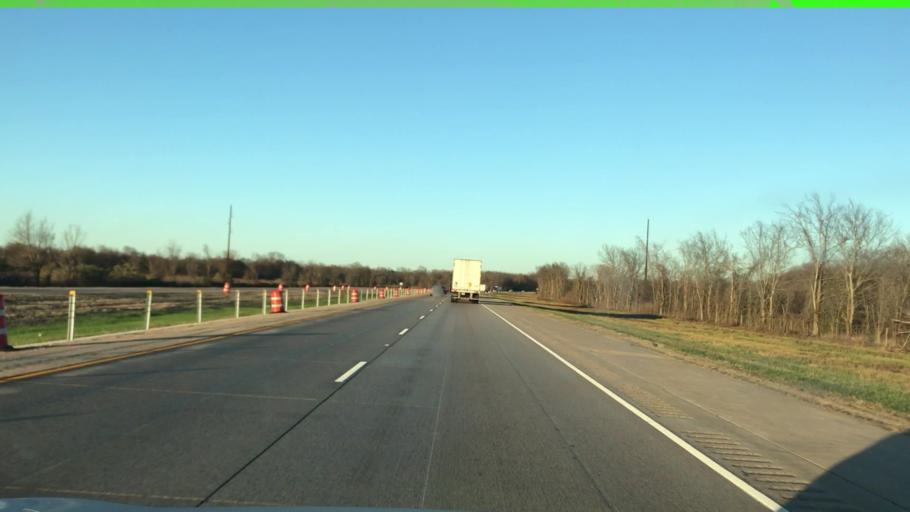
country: US
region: Arkansas
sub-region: Miller County
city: Texarkana
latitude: 33.5807
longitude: -93.8432
